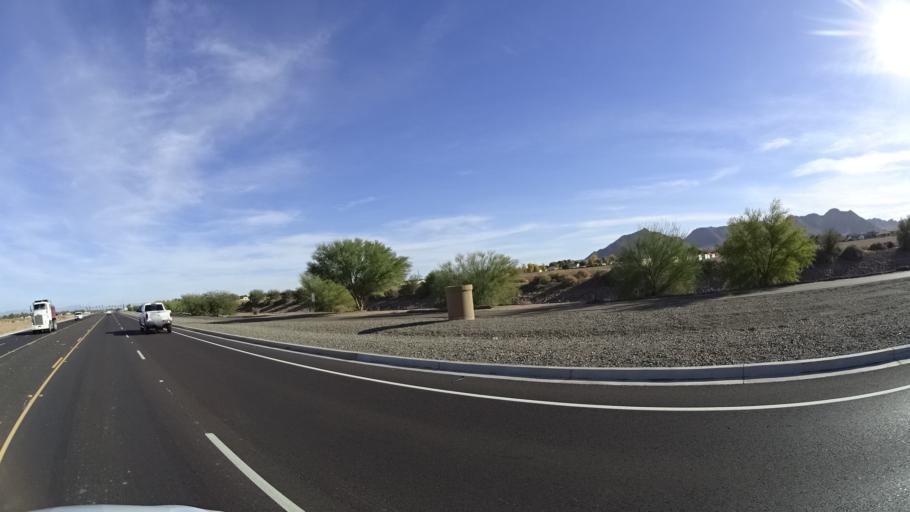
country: US
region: Arizona
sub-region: Maricopa County
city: Queen Creek
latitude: 33.2195
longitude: -111.6395
